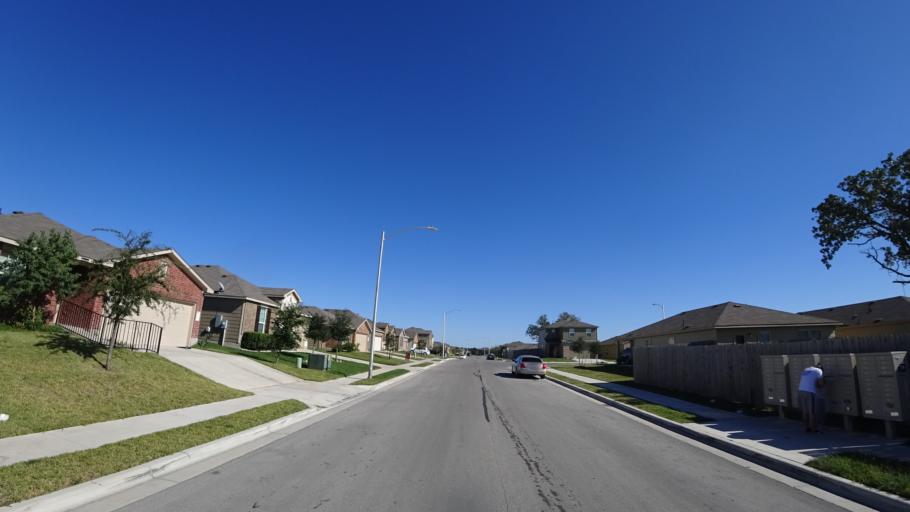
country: US
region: Texas
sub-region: Travis County
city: Hornsby Bend
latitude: 30.2796
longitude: -97.6260
